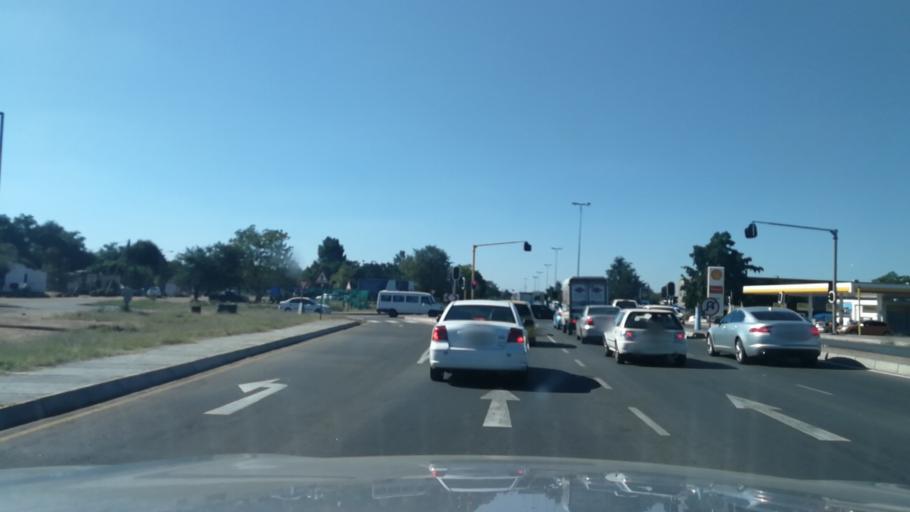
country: BW
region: South East
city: Gaborone
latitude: -24.6778
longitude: 25.9192
